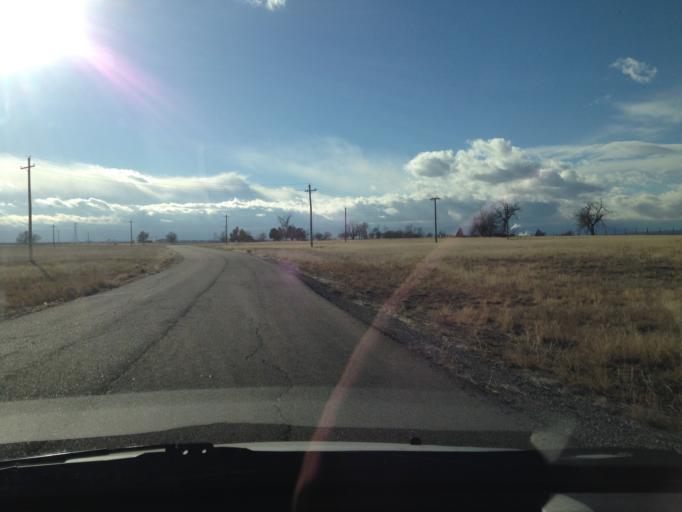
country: US
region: Colorado
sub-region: Adams County
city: Derby
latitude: 39.8308
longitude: -104.8621
